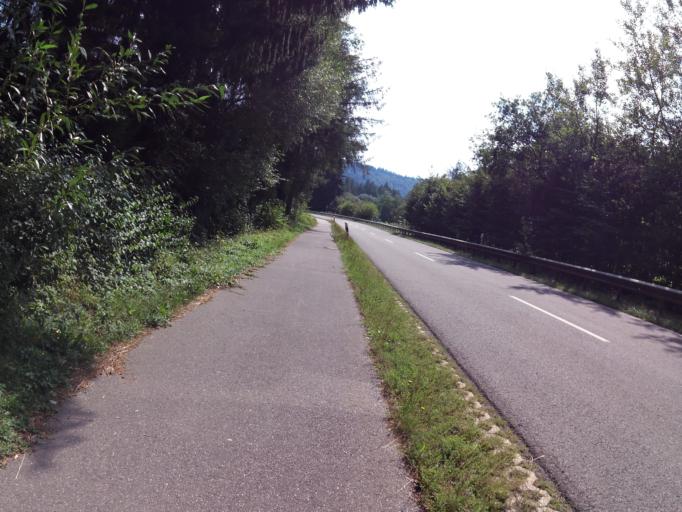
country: DE
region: Rheinland-Pfalz
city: Orenhofen
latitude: 49.8670
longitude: 6.6434
